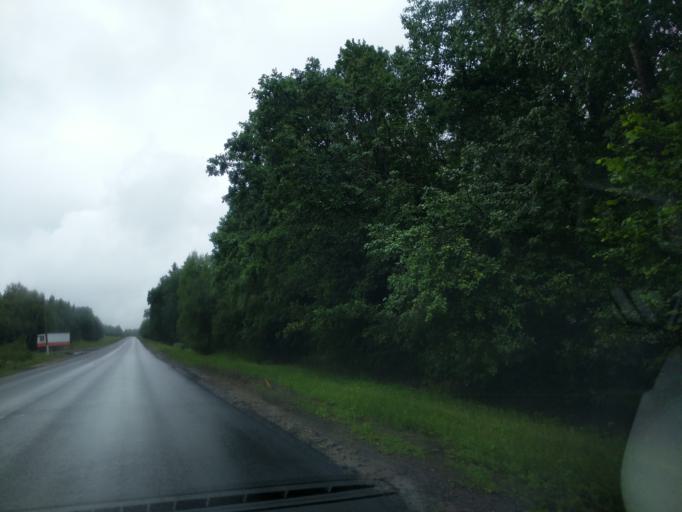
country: BY
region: Minsk
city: Syomkava
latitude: 54.2387
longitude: 27.4851
